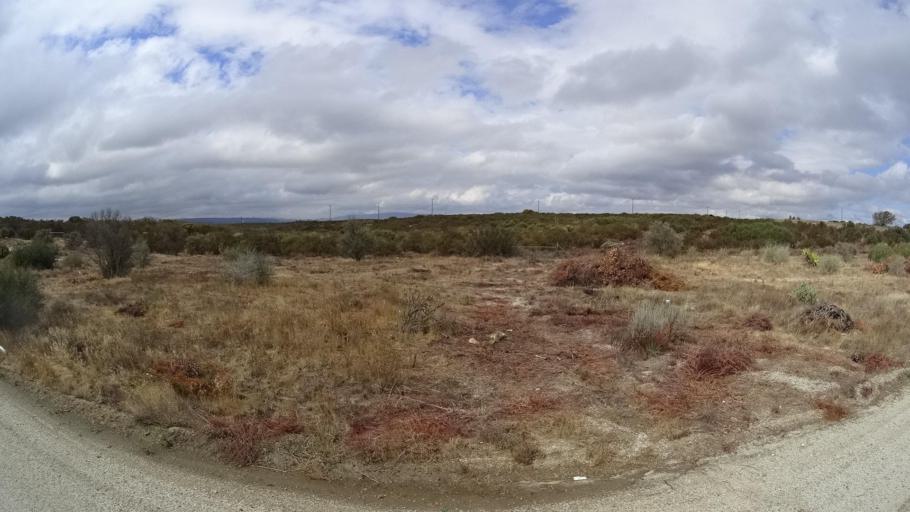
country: US
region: California
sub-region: San Diego County
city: Campo
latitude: 32.6564
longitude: -116.3150
